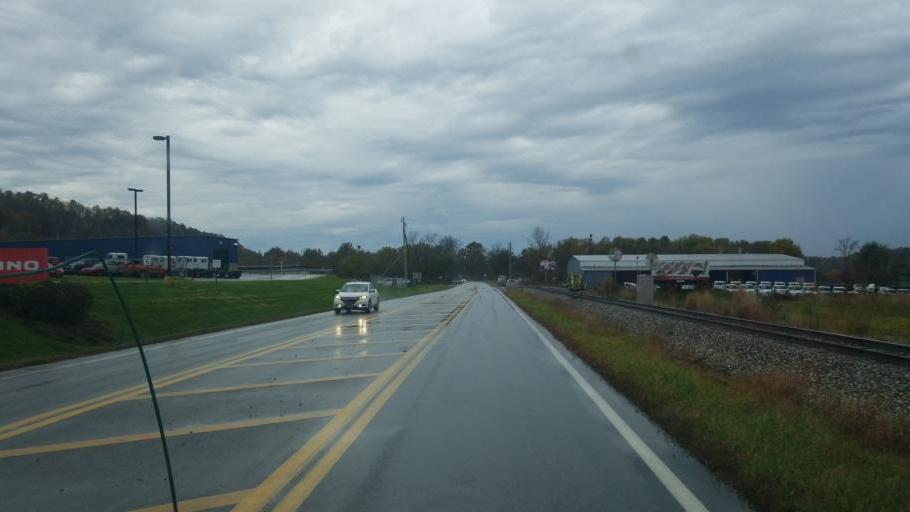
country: US
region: West Virginia
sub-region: Wood County
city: Williamstown
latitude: 39.3948
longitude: -81.4704
